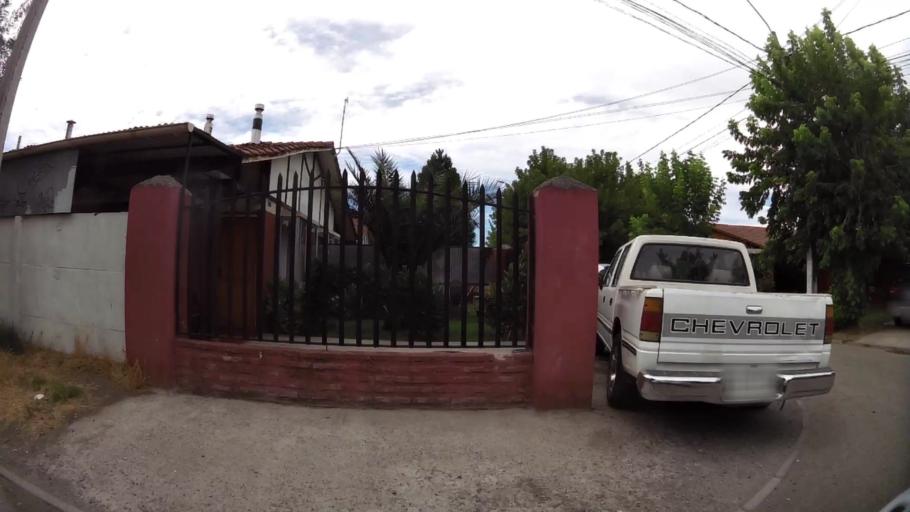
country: CL
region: O'Higgins
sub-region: Provincia de Cachapoal
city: Graneros
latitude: -34.0656
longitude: -70.7223
